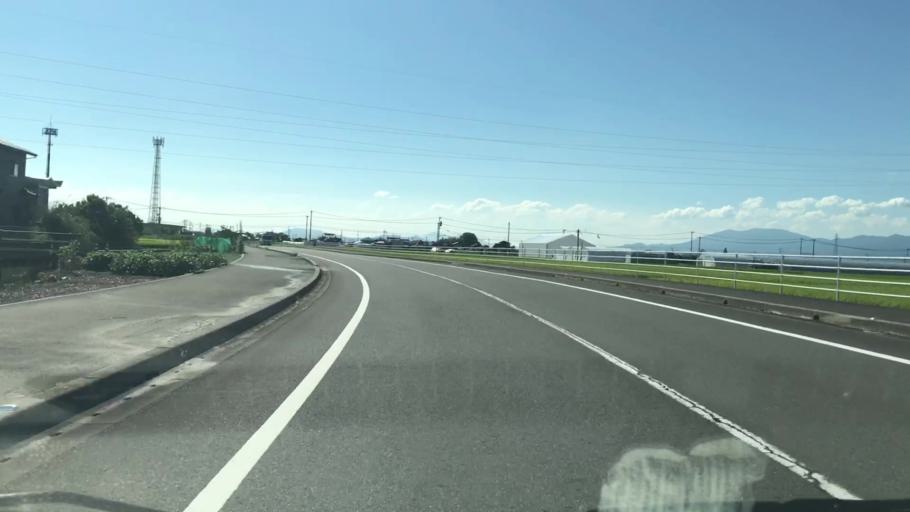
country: JP
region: Saga Prefecture
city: Okawa
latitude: 33.2305
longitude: 130.3659
